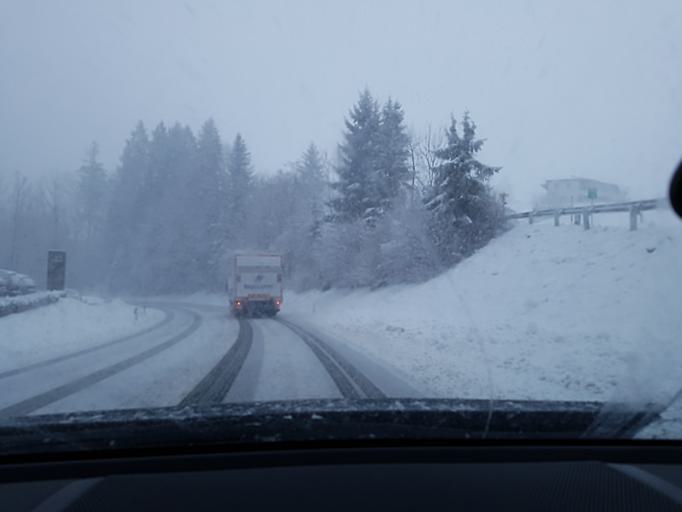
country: AT
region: Salzburg
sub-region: Politischer Bezirk Hallein
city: Abtenau
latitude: 47.5840
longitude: 13.3221
